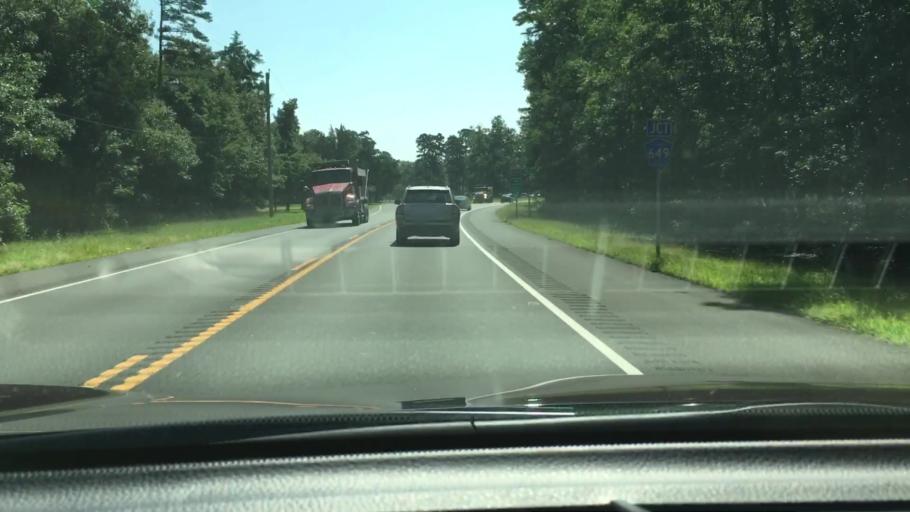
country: US
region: New Jersey
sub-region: Cape May County
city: Woodbine
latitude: 39.3128
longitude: -74.8254
